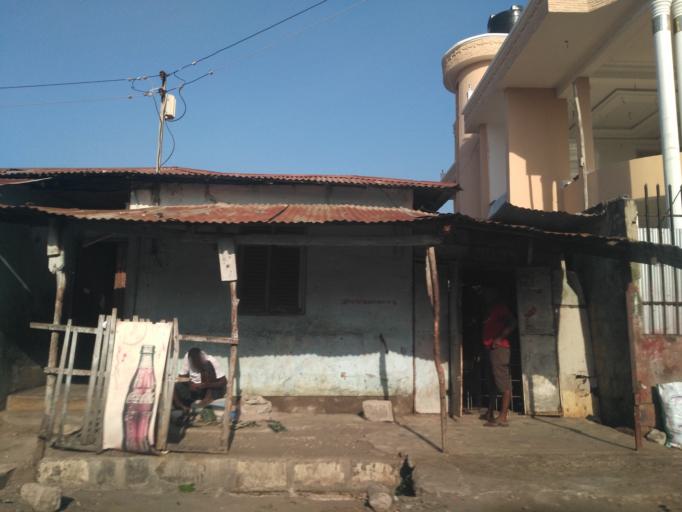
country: TZ
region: Dar es Salaam
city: Magomeni
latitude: -6.7865
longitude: 39.2648
